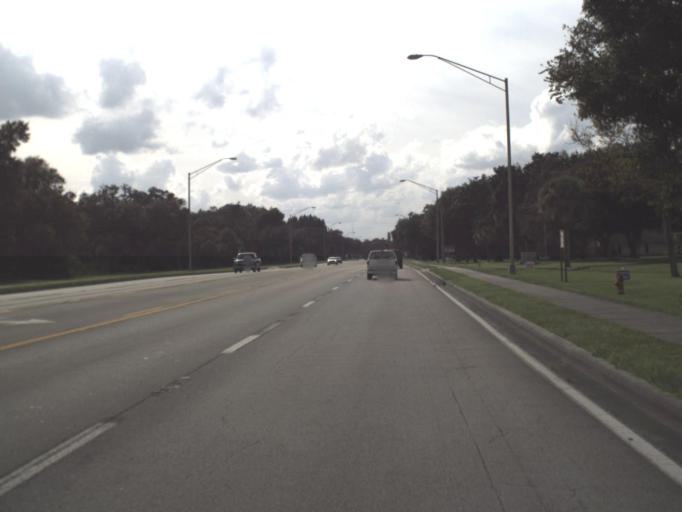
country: US
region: Florida
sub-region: Hendry County
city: LaBelle
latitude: 26.7618
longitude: -81.4281
